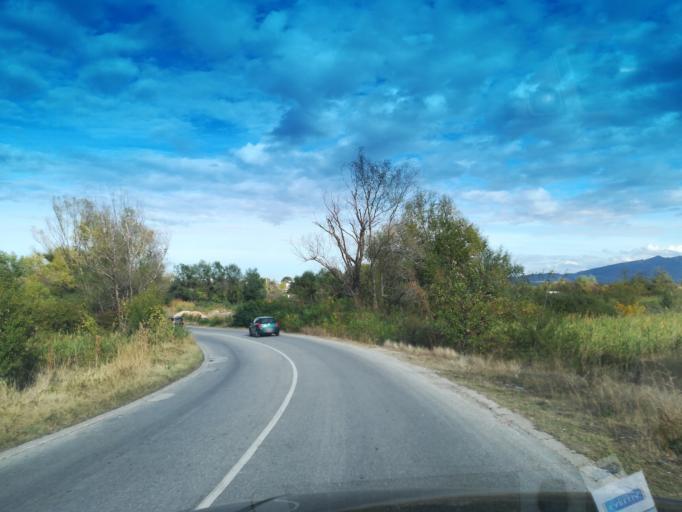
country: BG
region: Pazardzhik
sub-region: Obshtina Peshtera
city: Peshtera
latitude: 42.0464
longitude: 24.3087
